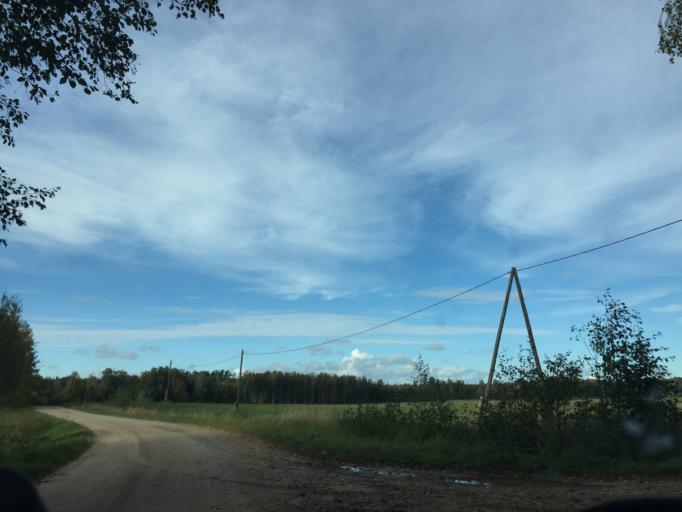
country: LV
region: Jaunpils
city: Jaunpils
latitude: 56.6142
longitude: 23.0414
